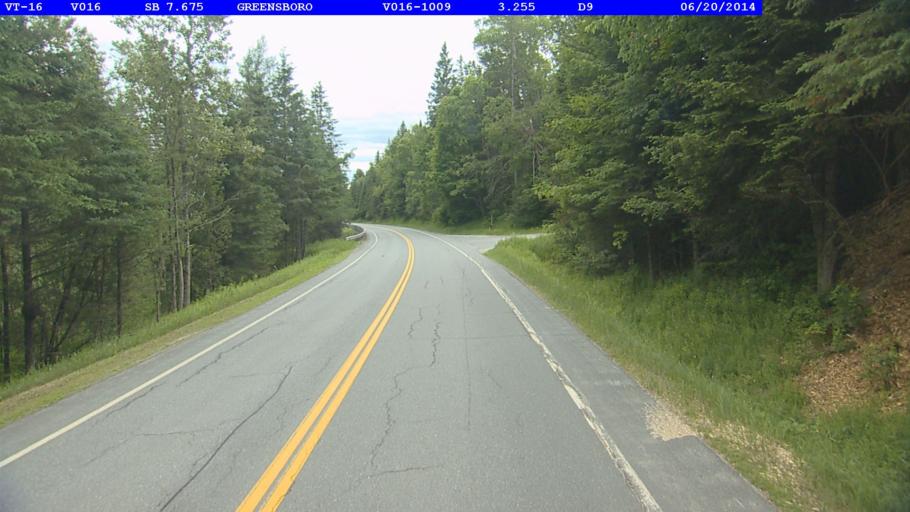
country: US
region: Vermont
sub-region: Caledonia County
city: Hardwick
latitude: 44.5861
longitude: -72.2394
